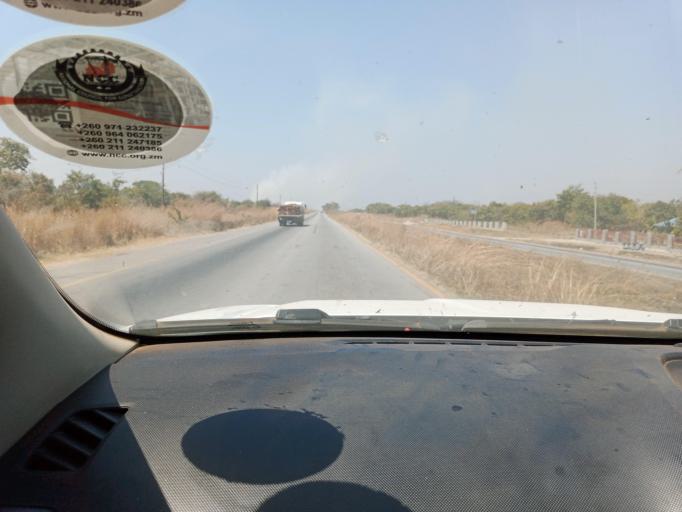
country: ZM
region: Copperbelt
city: Kitwe
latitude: -12.9149
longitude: 28.3444
